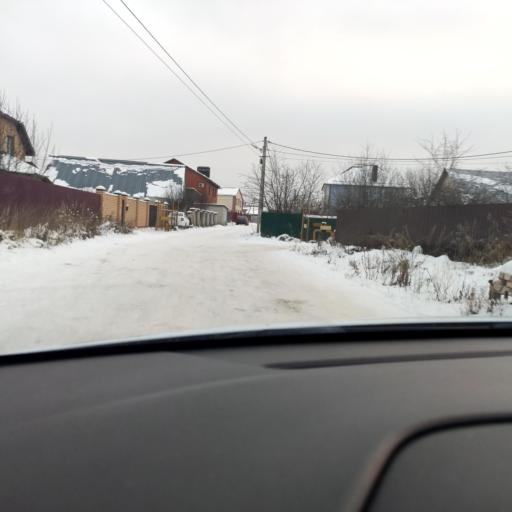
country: RU
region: Tatarstan
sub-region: Gorod Kazan'
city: Kazan
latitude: 55.8738
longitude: 49.1450
